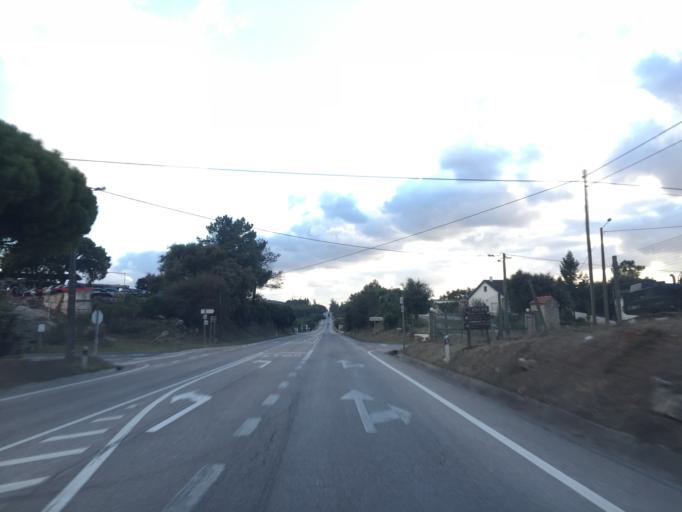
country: PT
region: Leiria
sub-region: Alcobaca
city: Turquel
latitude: 39.4814
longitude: -8.9365
